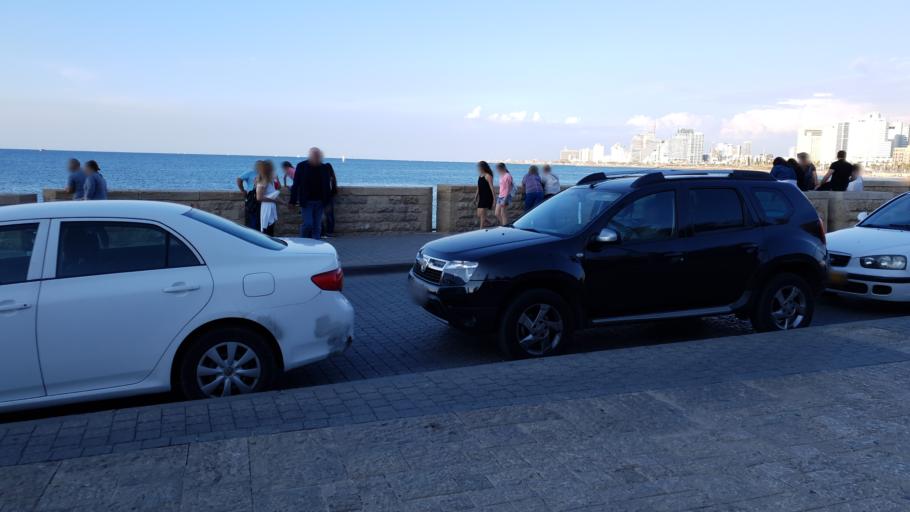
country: IL
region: Tel Aviv
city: Yafo
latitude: 32.0555
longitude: 34.7533
